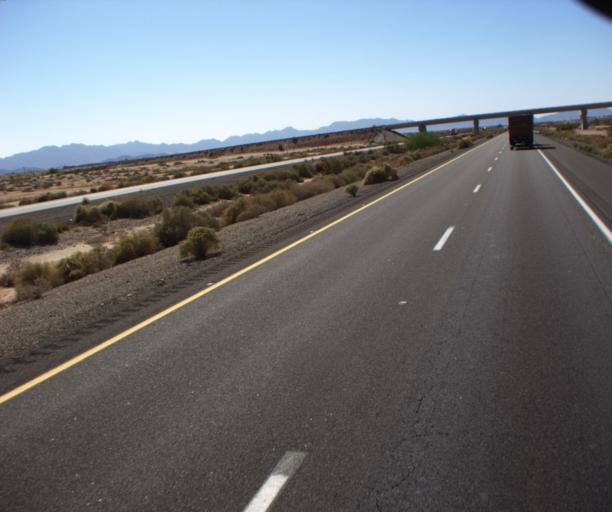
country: US
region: Arizona
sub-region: Yuma County
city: Wellton
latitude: 32.6748
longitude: -114.0706
